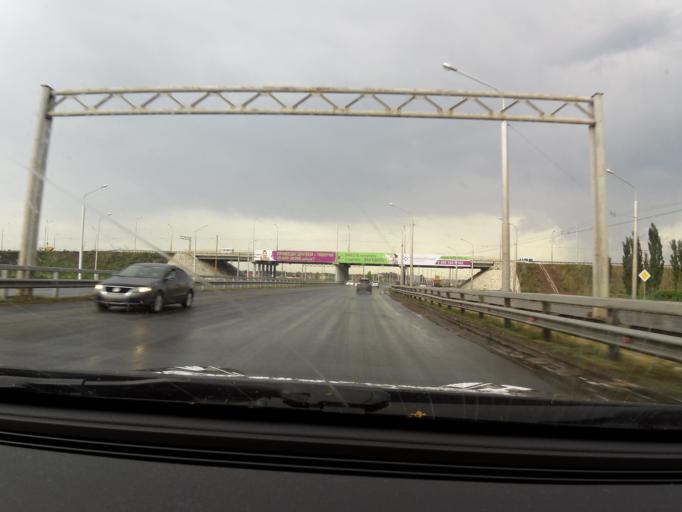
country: RU
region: Bashkortostan
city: Ufa
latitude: 54.7634
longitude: 55.9568
